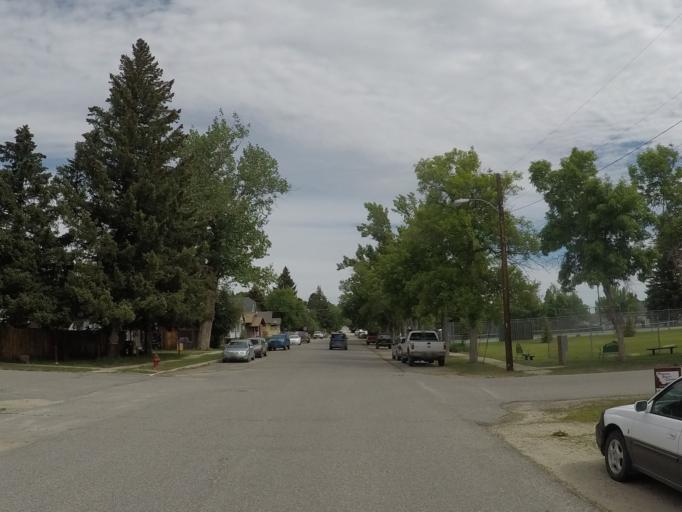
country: US
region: Montana
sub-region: Carbon County
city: Red Lodge
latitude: 45.1877
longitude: -109.2498
